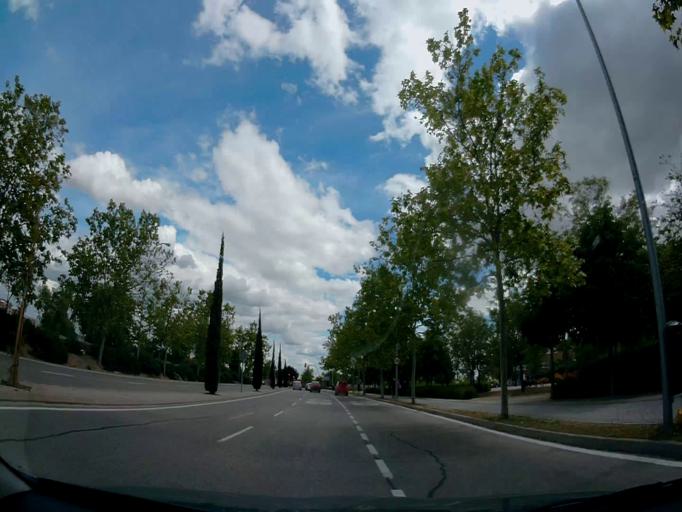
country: ES
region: Madrid
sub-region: Provincia de Madrid
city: Vicalvaro
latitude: 40.4041
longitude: -3.6171
